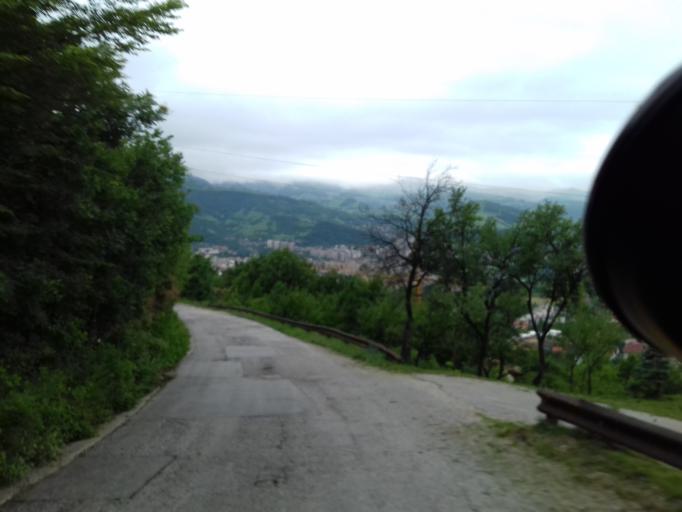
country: BA
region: Federation of Bosnia and Herzegovina
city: Zenica
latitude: 44.2155
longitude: 17.9326
